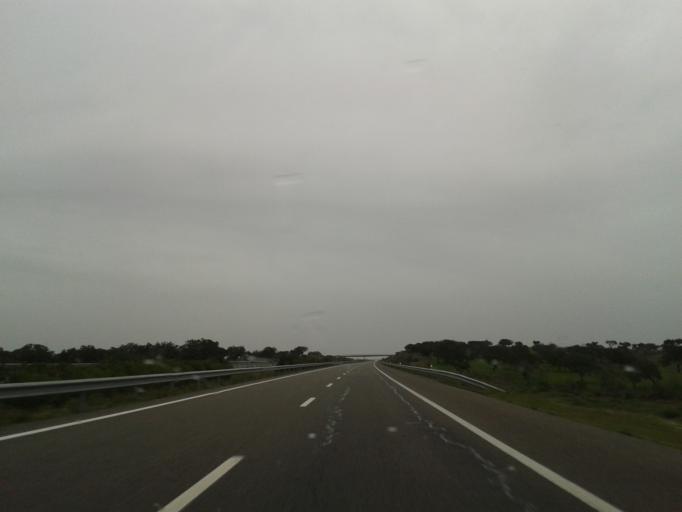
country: PT
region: Beja
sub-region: Ourique
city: Ourique
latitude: 37.5773
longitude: -8.1871
